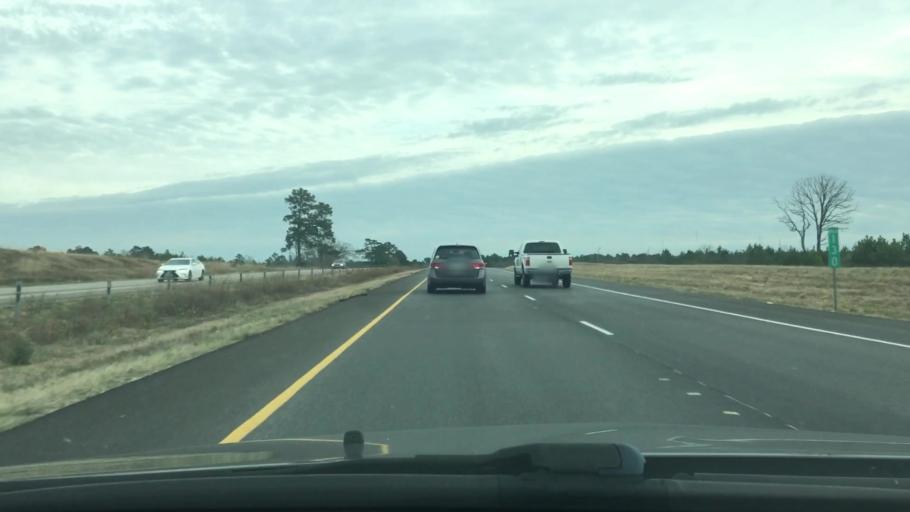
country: US
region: Texas
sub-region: Madison County
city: Madisonville
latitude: 30.8450
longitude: -95.7299
